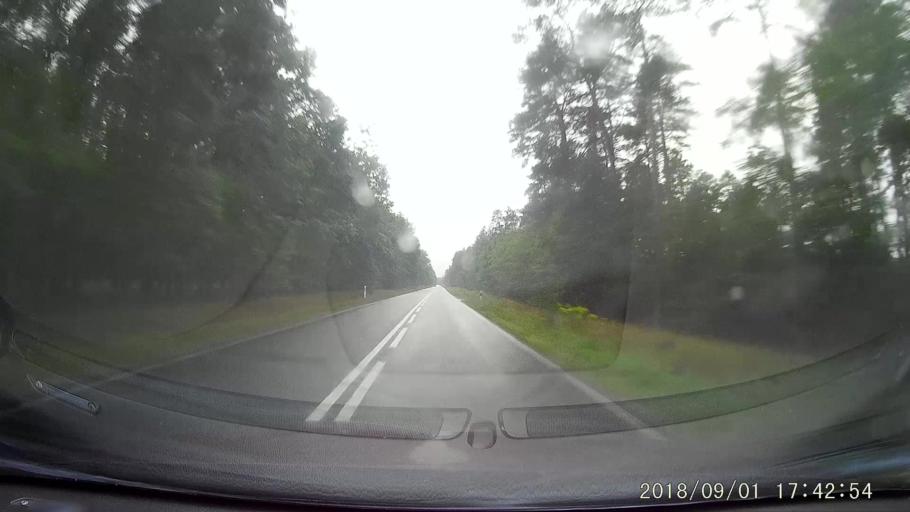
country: PL
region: Lubusz
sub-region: Powiat zaganski
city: Ilowa
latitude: 51.5507
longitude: 15.2551
